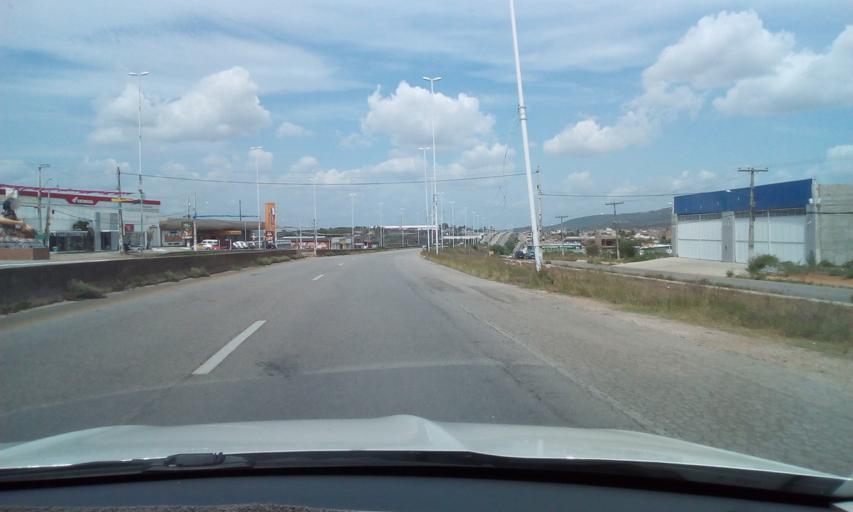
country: BR
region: Pernambuco
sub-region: Bezerros
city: Bezerros
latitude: -8.2387
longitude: -35.7457
